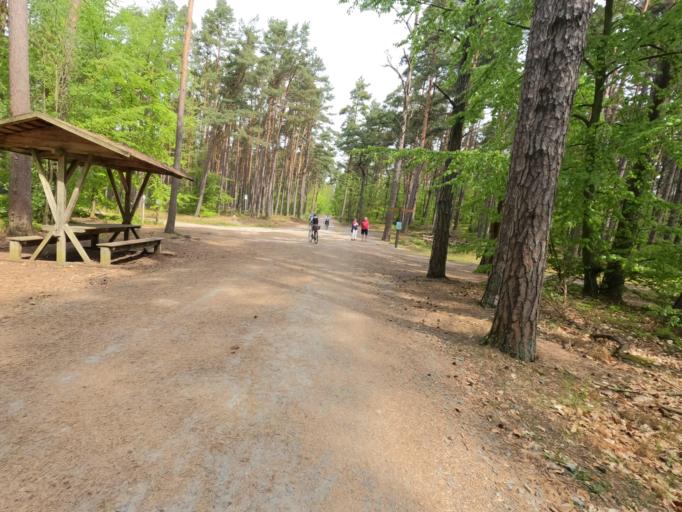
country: DE
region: Mecklenburg-Vorpommern
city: Ostseebad Prerow
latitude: 54.4627
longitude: 12.5153
